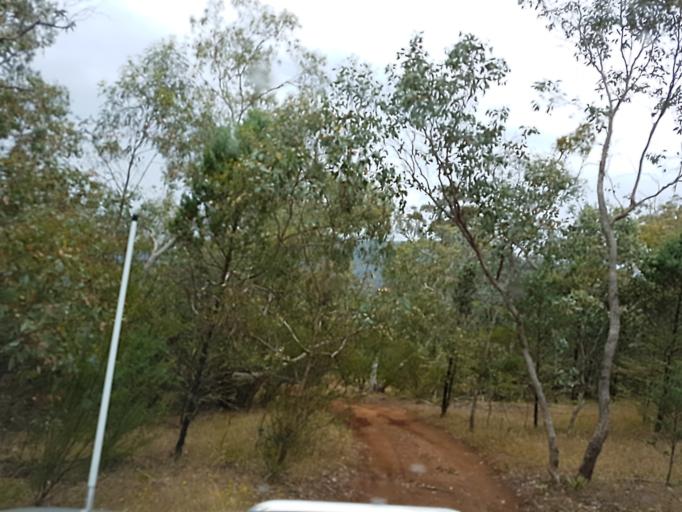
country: AU
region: New South Wales
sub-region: Snowy River
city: Jindabyne
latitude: -36.9426
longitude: 148.3951
